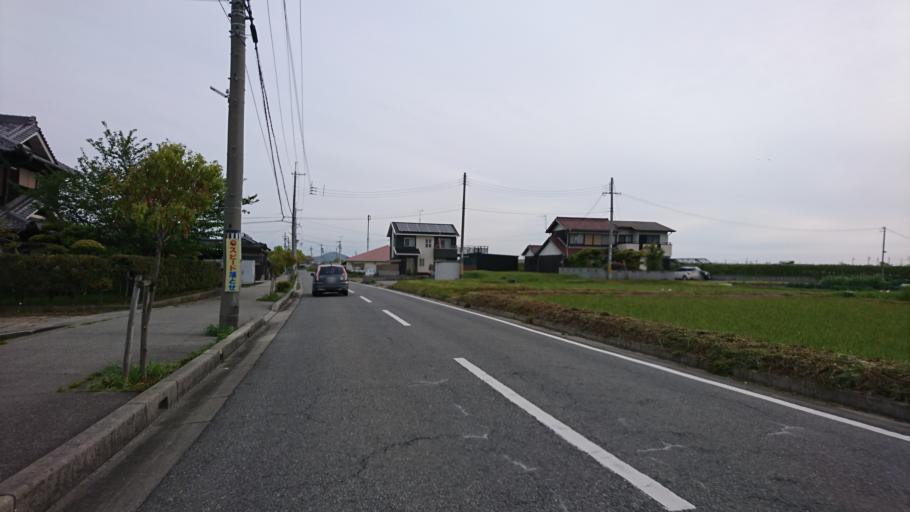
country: JP
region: Hyogo
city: Kakogawacho-honmachi
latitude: 34.7674
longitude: 134.9084
